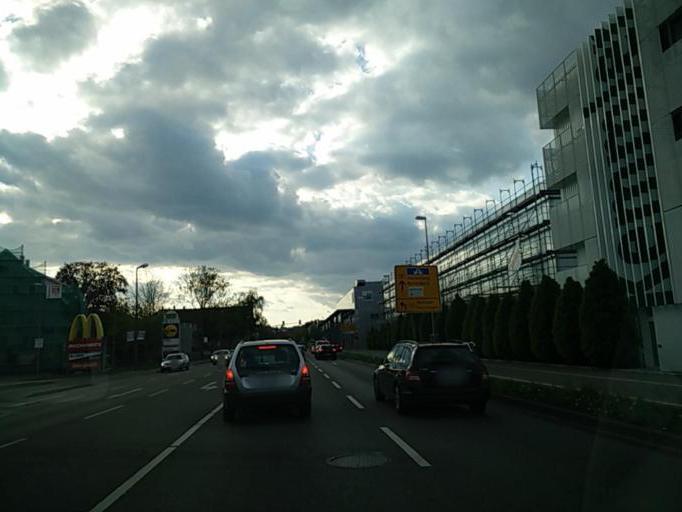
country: DE
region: Baden-Wuerttemberg
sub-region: Tuebingen Region
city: Tuebingen
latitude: 48.5137
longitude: 9.0722
